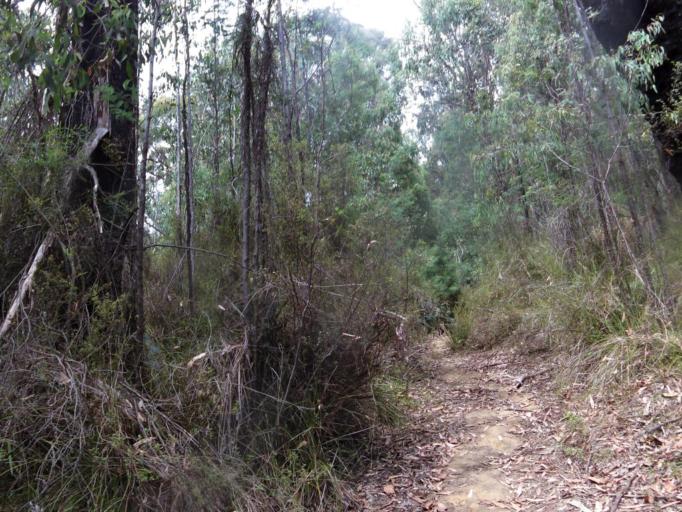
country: AU
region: Victoria
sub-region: Yarra Ranges
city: Healesville
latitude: -37.4513
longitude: 145.5844
